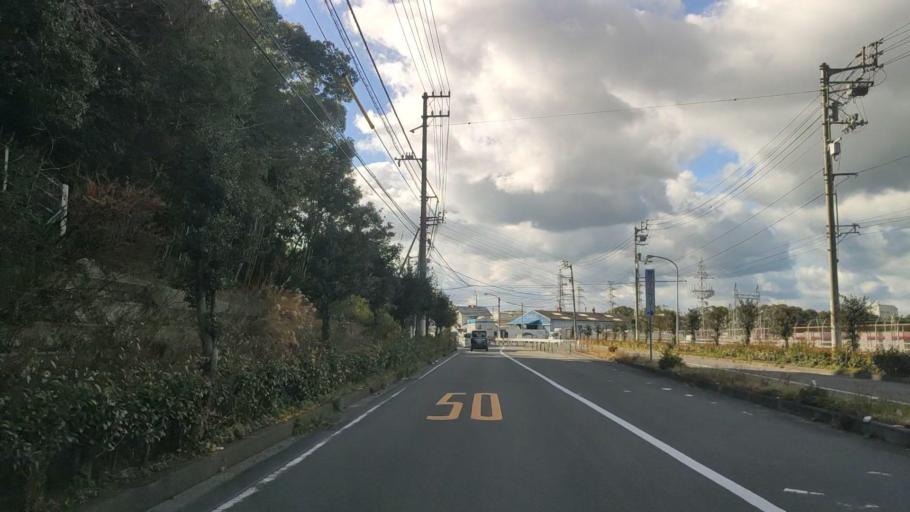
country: JP
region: Ehime
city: Masaki-cho
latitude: 33.8445
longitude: 132.7087
